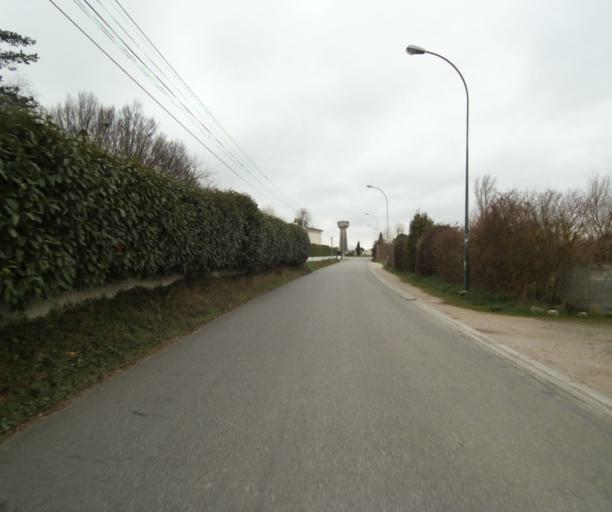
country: FR
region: Midi-Pyrenees
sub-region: Departement de l'Ariege
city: Mazeres
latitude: 43.2482
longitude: 1.6722
